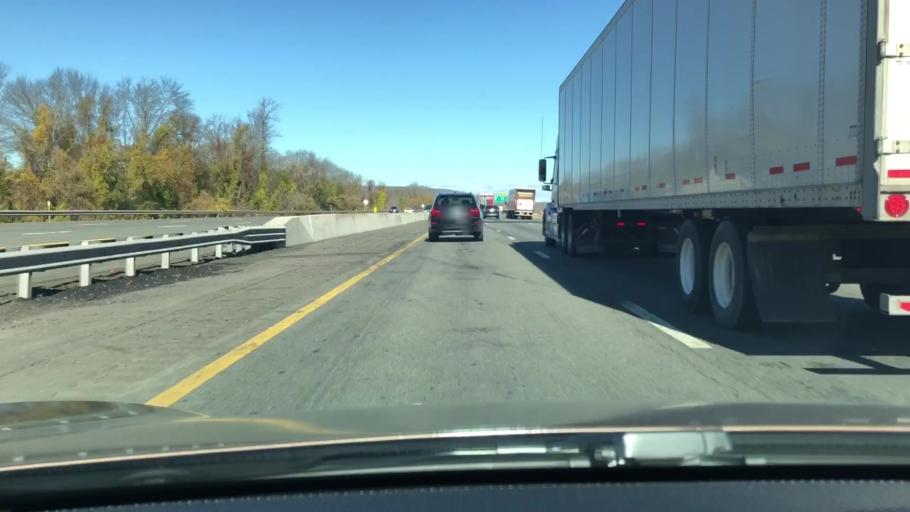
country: US
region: New York
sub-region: Orange County
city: Harriman
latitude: 41.2910
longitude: -74.1397
